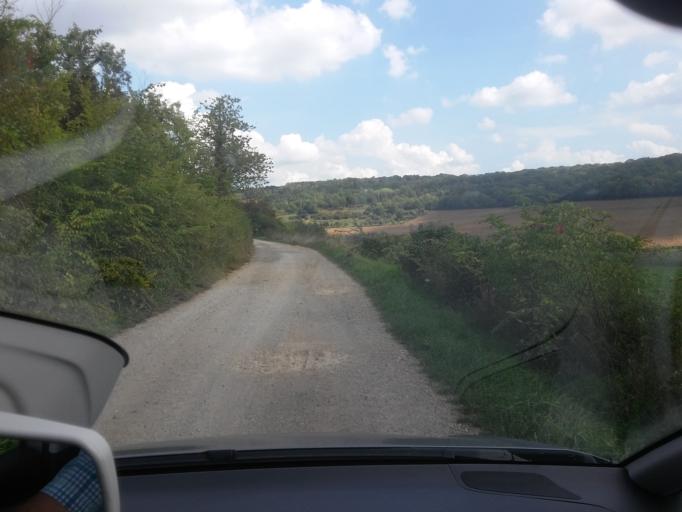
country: FR
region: Lorraine
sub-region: Departement de la Meuse
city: Montmedy
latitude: 49.5050
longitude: 5.3946
